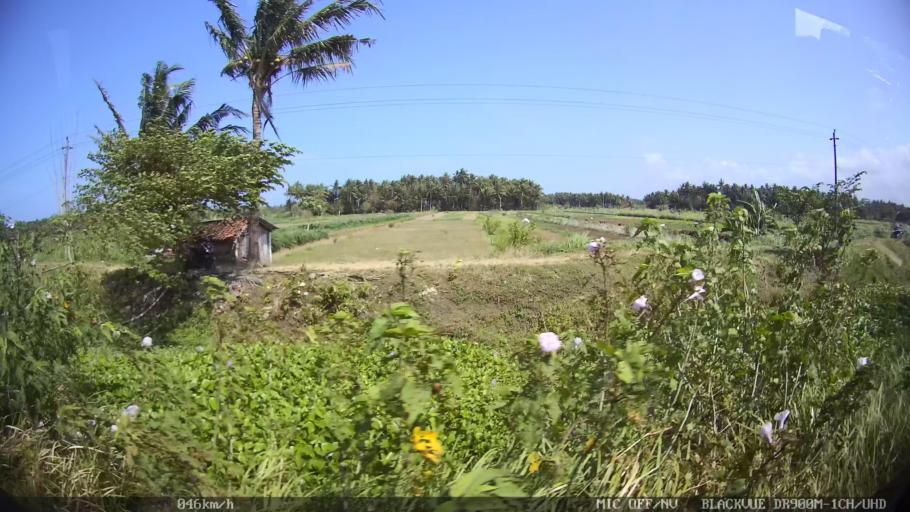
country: ID
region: Daerah Istimewa Yogyakarta
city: Srandakan
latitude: -7.9318
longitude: 110.1556
